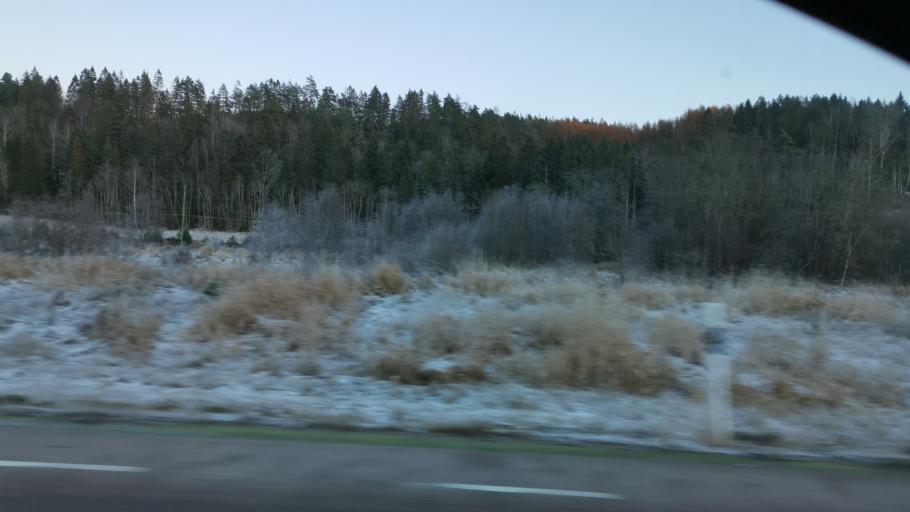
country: SE
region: Vaestra Goetaland
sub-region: Munkedals Kommun
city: Munkedal
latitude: 58.4227
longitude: 11.7254
